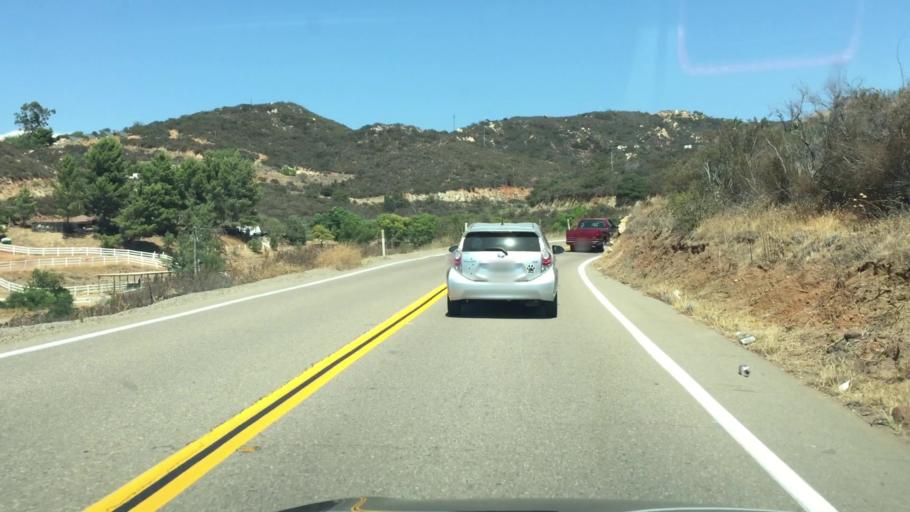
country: US
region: California
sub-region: San Diego County
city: Jamul
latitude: 32.7391
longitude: -116.8158
